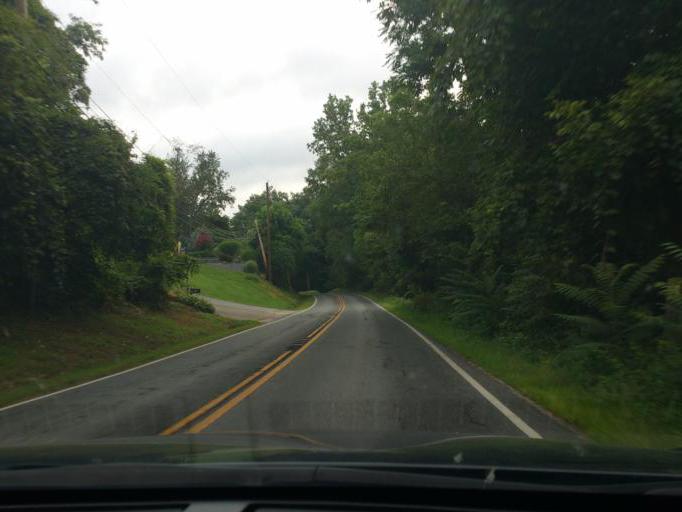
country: US
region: Maryland
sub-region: Cecil County
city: Rising Sun
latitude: 39.6568
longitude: -76.1467
